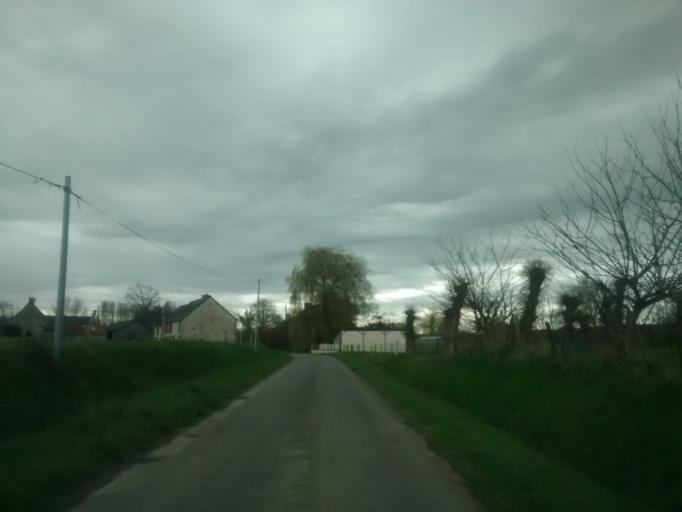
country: FR
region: Brittany
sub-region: Departement d'Ille-et-Vilaine
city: Gosne
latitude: 48.2474
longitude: -1.4836
